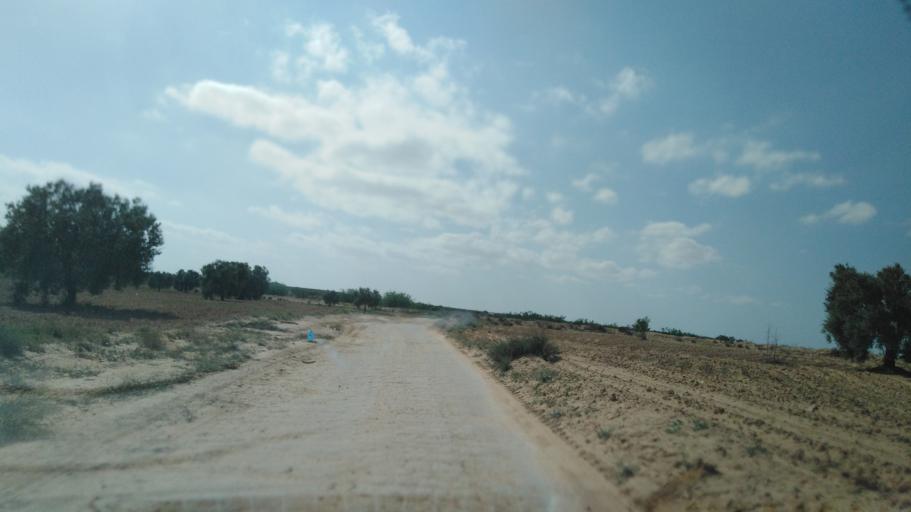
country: TN
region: Safaqis
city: Bi'r `Ali Bin Khalifah
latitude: 34.8003
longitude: 10.3809
